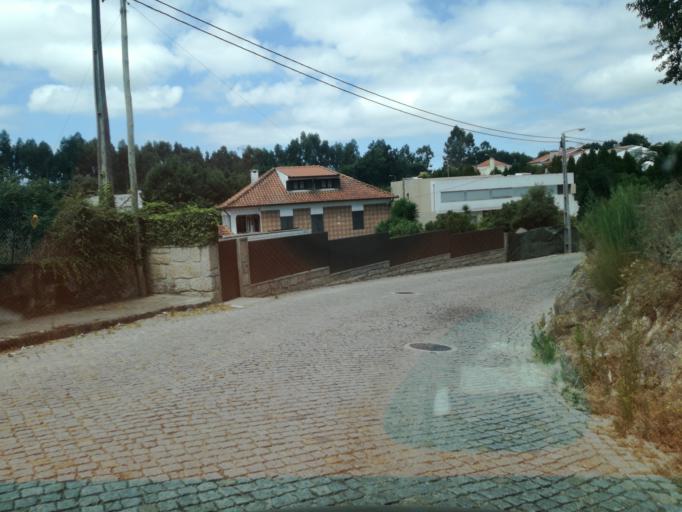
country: PT
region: Porto
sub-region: Maia
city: Nogueira
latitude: 41.2404
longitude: -8.5959
